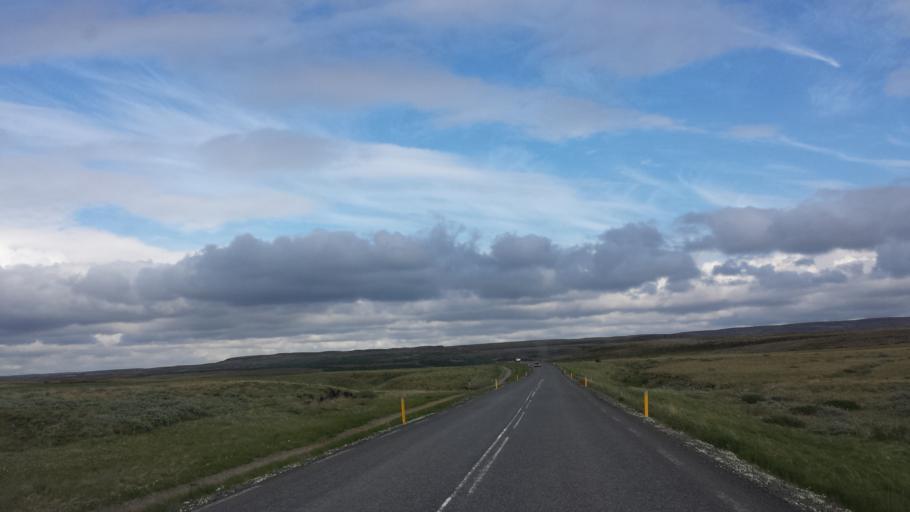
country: IS
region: South
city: Vestmannaeyjar
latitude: 64.3062
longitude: -20.1888
